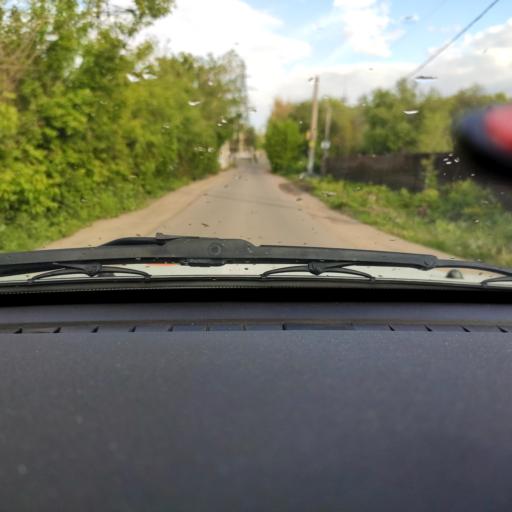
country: RU
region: Voronezj
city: Maslovka
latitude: 51.5837
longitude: 39.1618
